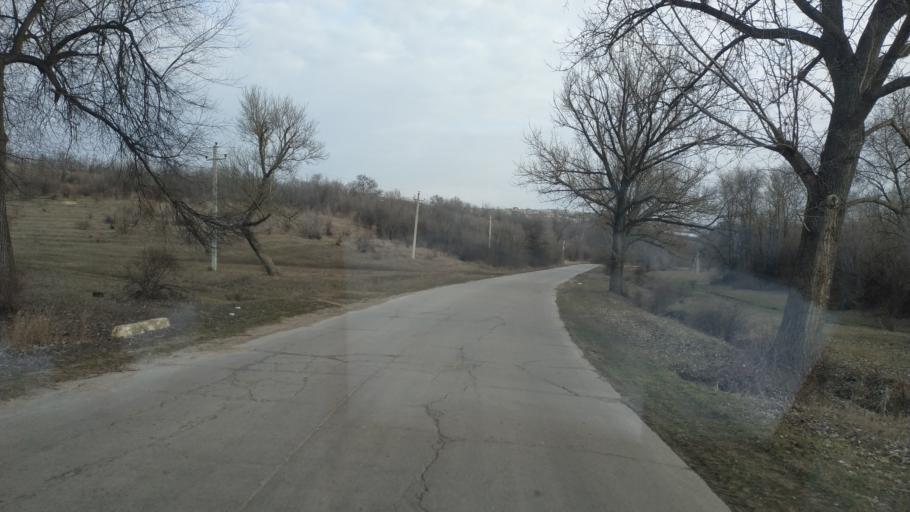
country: MD
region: Chisinau
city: Vadul lui Voda
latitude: 47.0048
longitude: 29.1123
